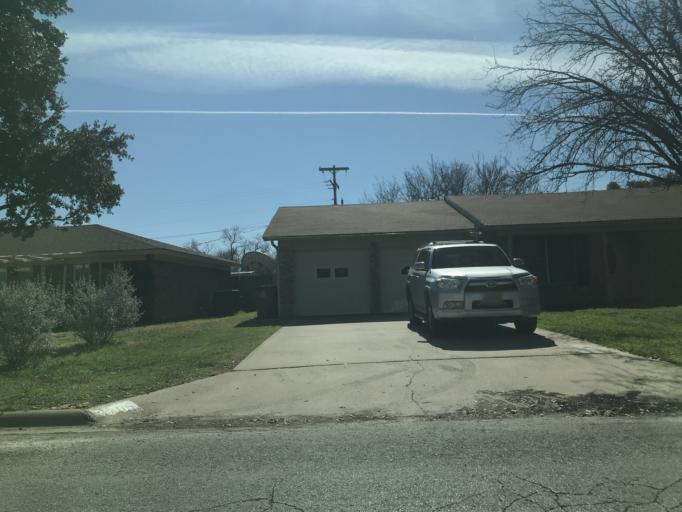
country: US
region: Texas
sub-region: Tom Green County
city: San Angelo
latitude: 31.4350
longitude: -100.4872
